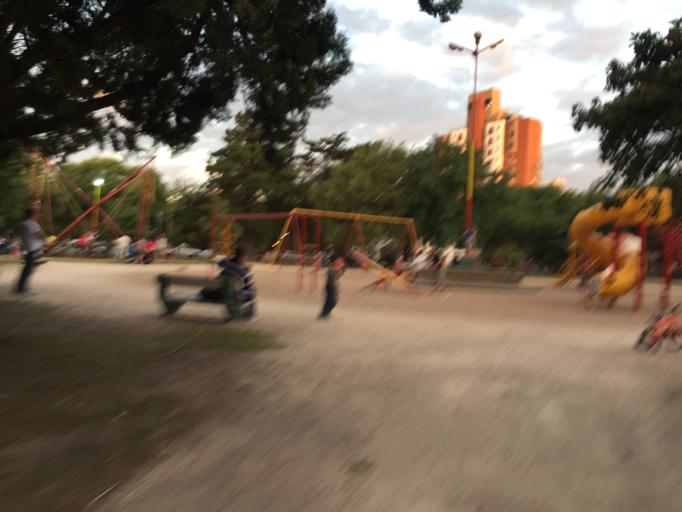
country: AR
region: Buenos Aires
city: Miramar
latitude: -38.2713
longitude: -57.8400
